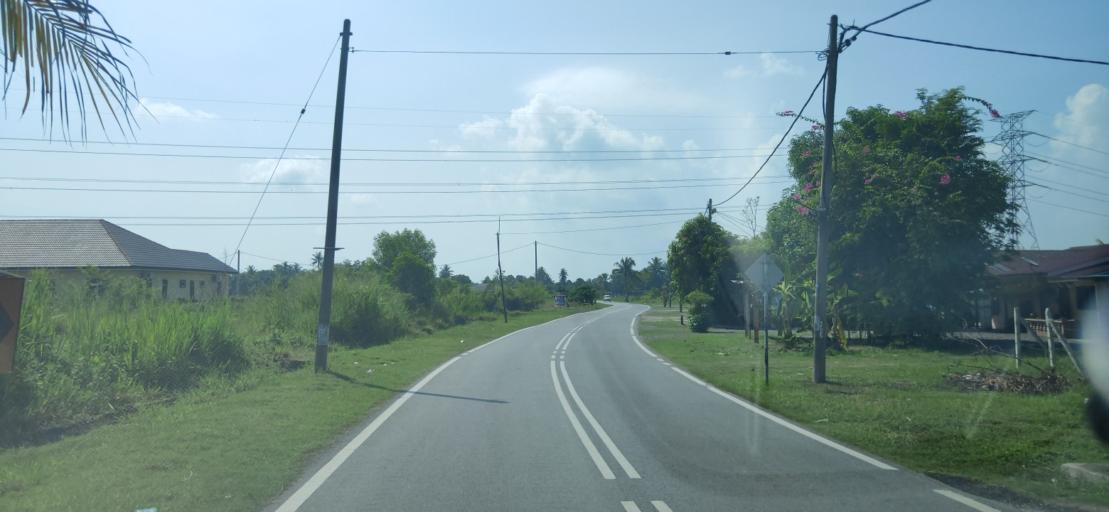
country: MY
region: Kedah
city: Sungai Petani
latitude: 5.6597
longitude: 100.4701
